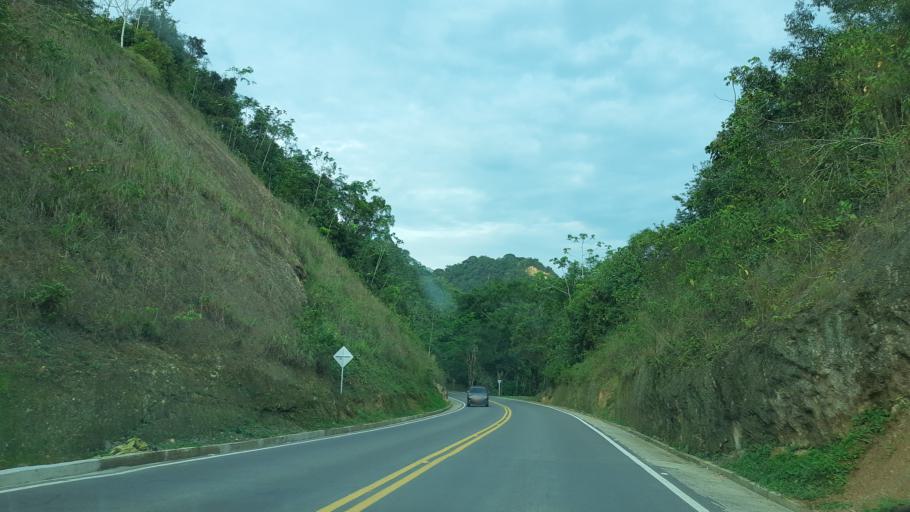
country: CO
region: Boyaca
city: San Luis de Gaceno
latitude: 4.8297
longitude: -73.1588
